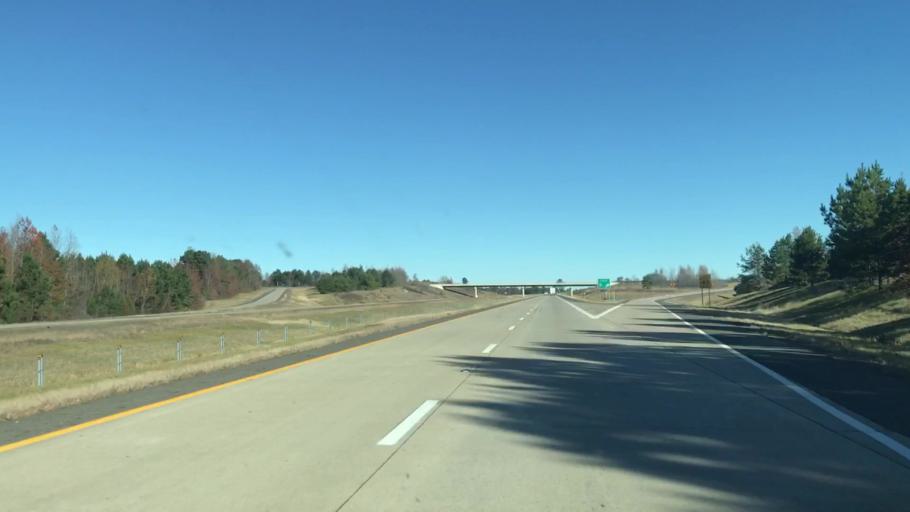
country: US
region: Texas
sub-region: Cass County
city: Queen City
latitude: 33.1155
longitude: -93.8940
